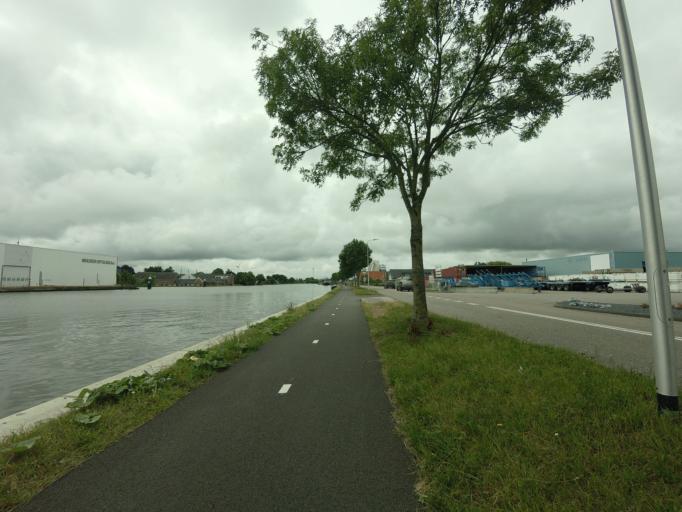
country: NL
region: South Holland
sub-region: Gemeente Alphen aan den Rijn
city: Alphen aan den Rijn
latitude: 52.1370
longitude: 4.6253
